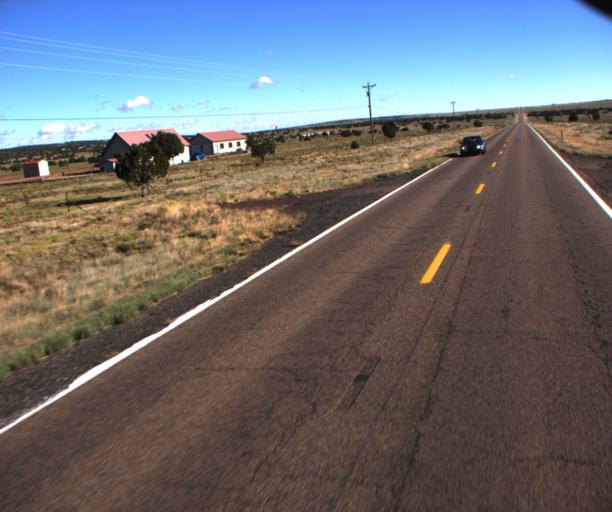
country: US
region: Arizona
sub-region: Navajo County
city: White Mountain Lake
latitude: 34.3420
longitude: -109.7313
